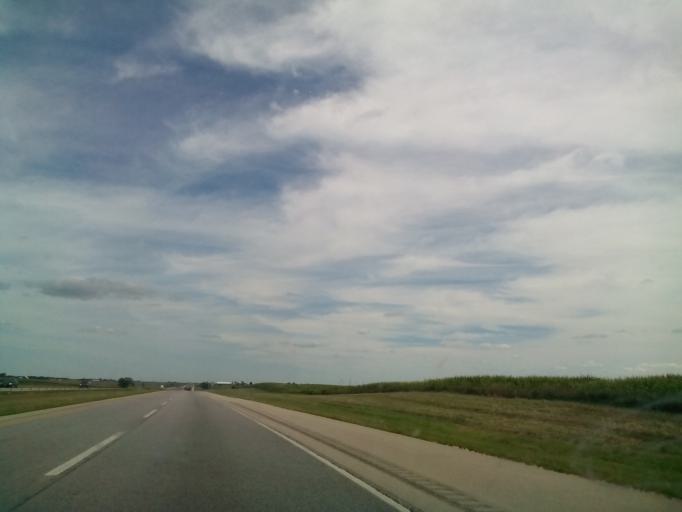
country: US
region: Illinois
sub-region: DeKalb County
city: Malta
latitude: 41.8992
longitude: -88.9503
